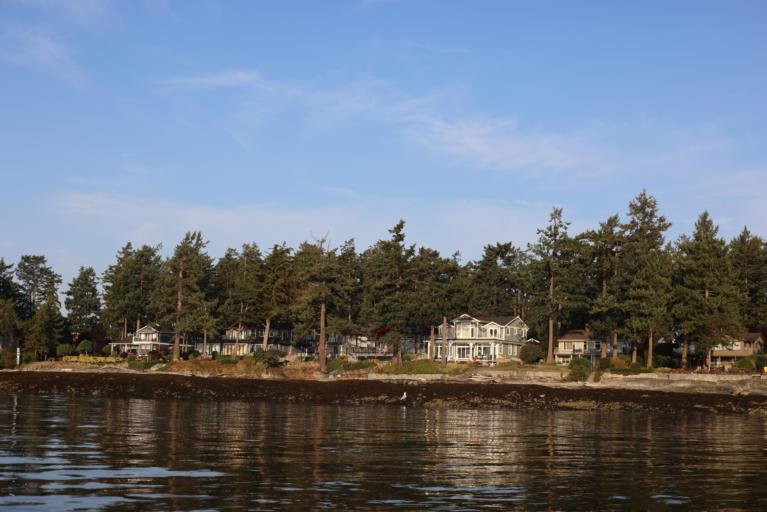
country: CA
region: British Columbia
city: North Saanich
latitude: 48.6614
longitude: -123.3904
